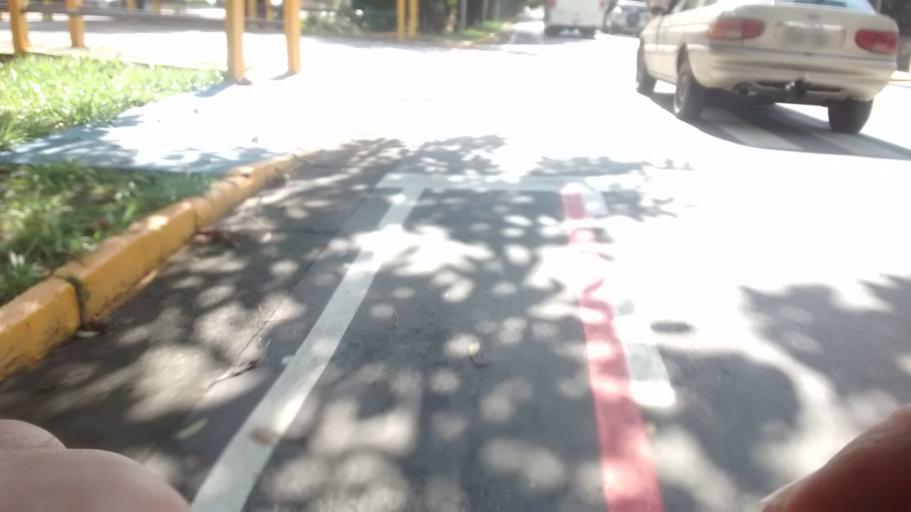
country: BR
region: Minas Gerais
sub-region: Itajuba
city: Itajuba
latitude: -22.4174
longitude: -45.4545
